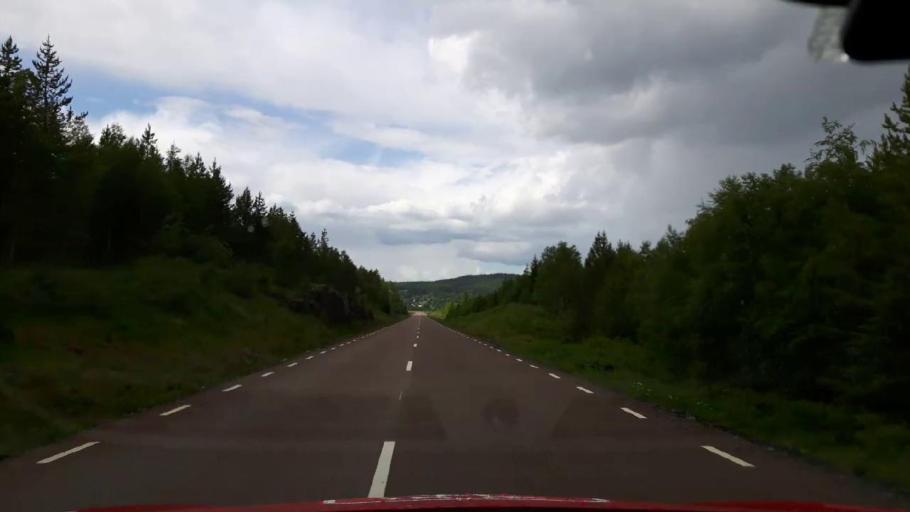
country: SE
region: Jaemtland
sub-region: Krokoms Kommun
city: Valla
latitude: 63.8956
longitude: 14.2560
